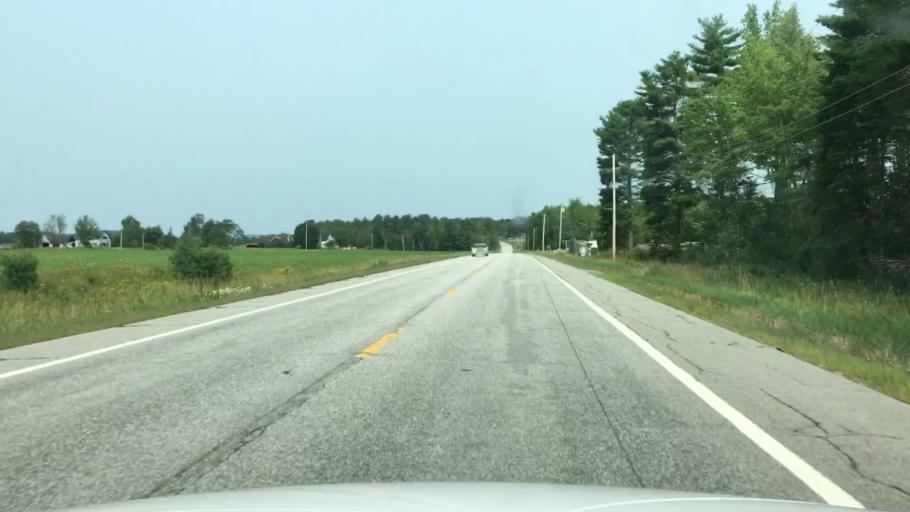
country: US
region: Maine
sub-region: Kennebec County
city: Wayne
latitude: 44.3886
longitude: -70.1107
